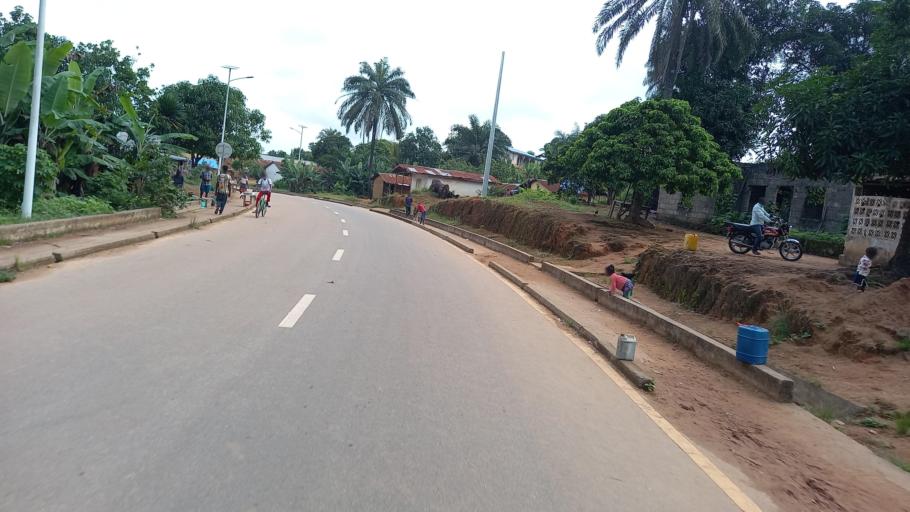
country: SL
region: Eastern Province
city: Kailahun
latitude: 8.2868
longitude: -10.5733
